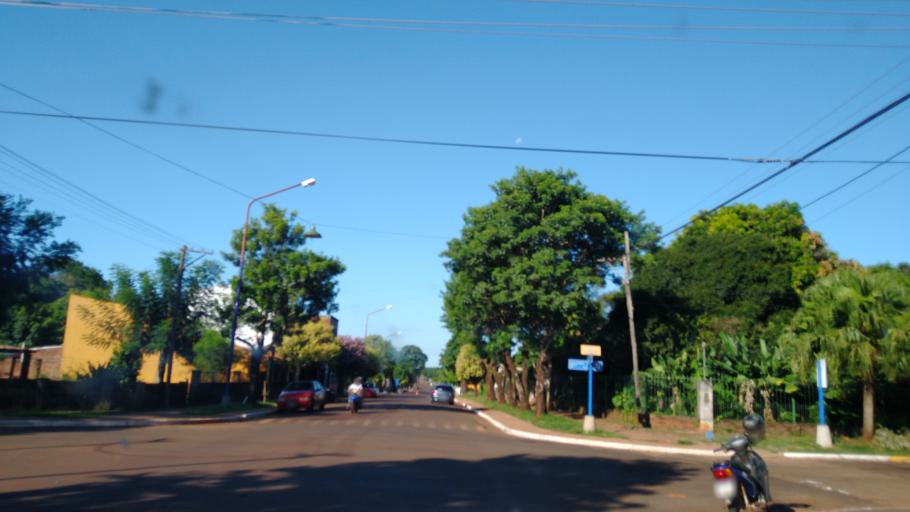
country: AR
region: Misiones
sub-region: Departamento de San Ignacio
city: San Ignacio
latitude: -27.2537
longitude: -55.5346
